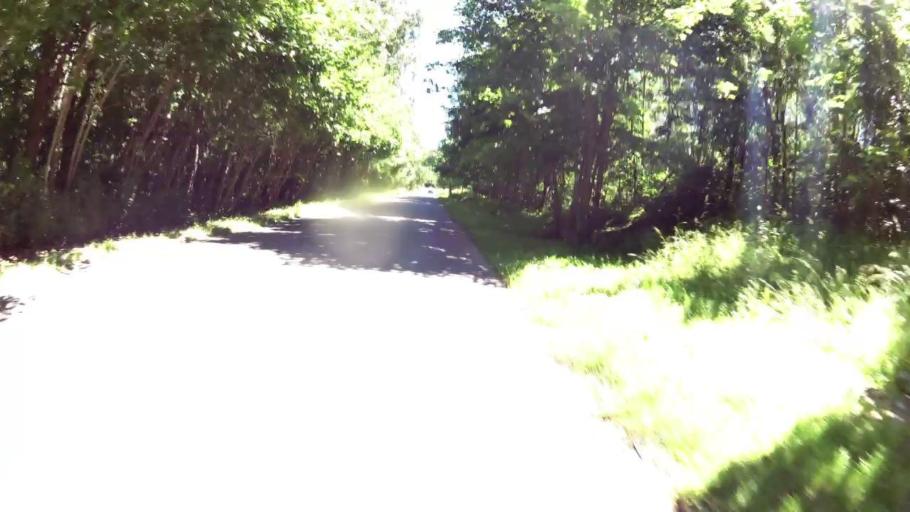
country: PL
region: West Pomeranian Voivodeship
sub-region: Powiat gryficki
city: Rewal
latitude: 54.0891
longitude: 15.0419
